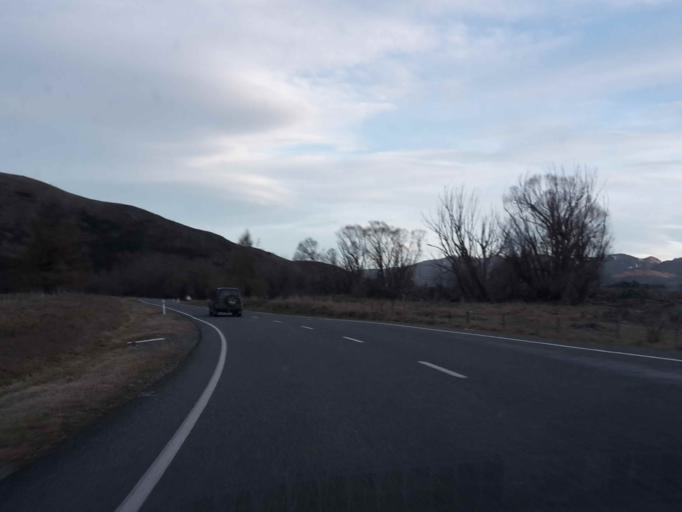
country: NZ
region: Canterbury
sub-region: Timaru District
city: Pleasant Point
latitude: -44.0718
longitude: 170.6667
